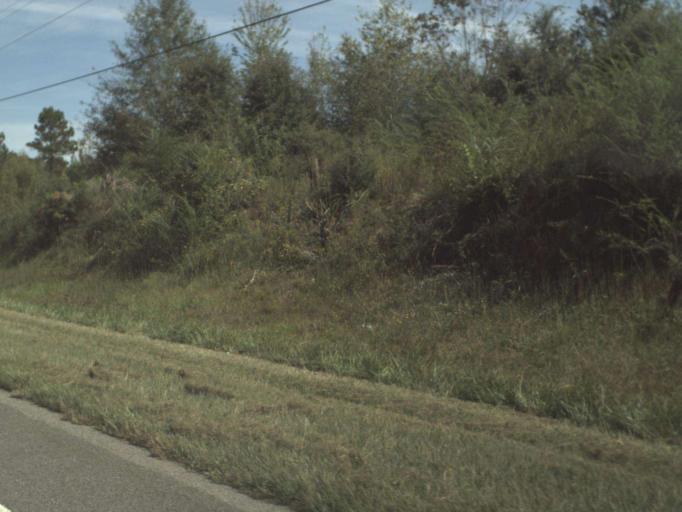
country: US
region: Florida
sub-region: Washington County
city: Chipley
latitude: 30.6860
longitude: -85.5681
